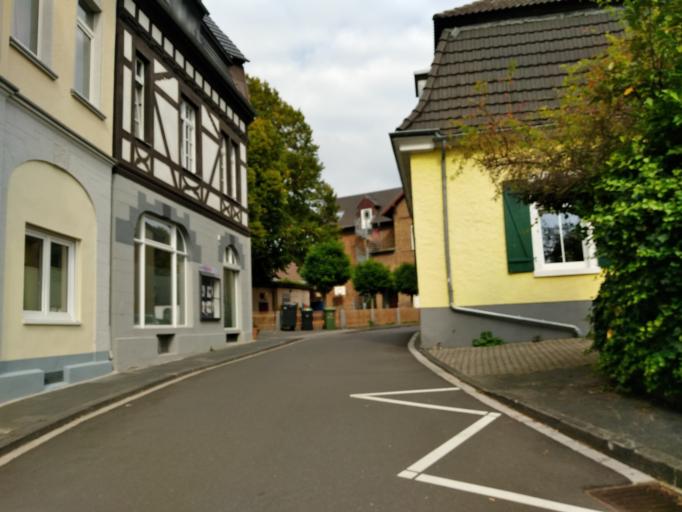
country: DE
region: North Rhine-Westphalia
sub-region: Regierungsbezirk Koln
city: Bad Honnef
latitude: 50.6576
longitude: 7.2115
